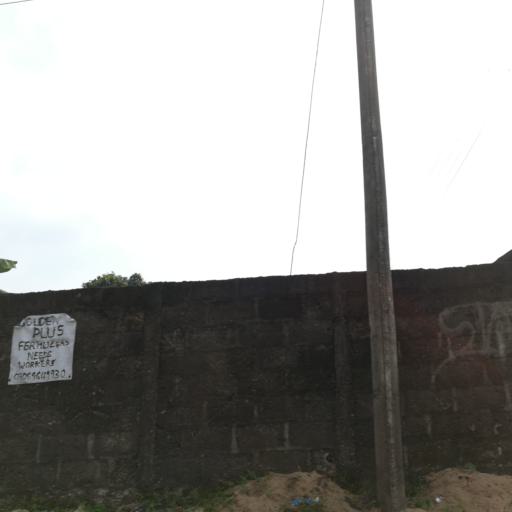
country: NG
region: Rivers
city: Port Harcourt
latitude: 4.8381
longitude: 7.0665
